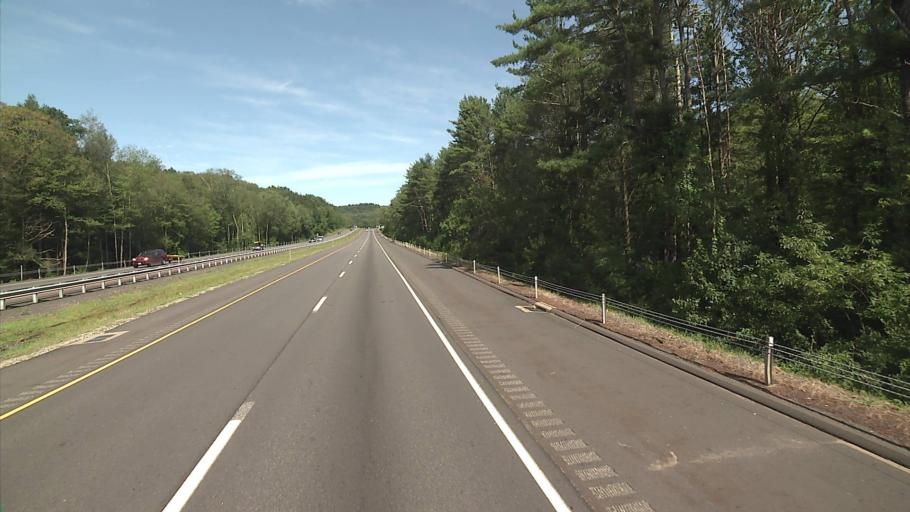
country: US
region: Connecticut
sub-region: Hartford County
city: Terramuggus
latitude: 41.6052
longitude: -72.4235
